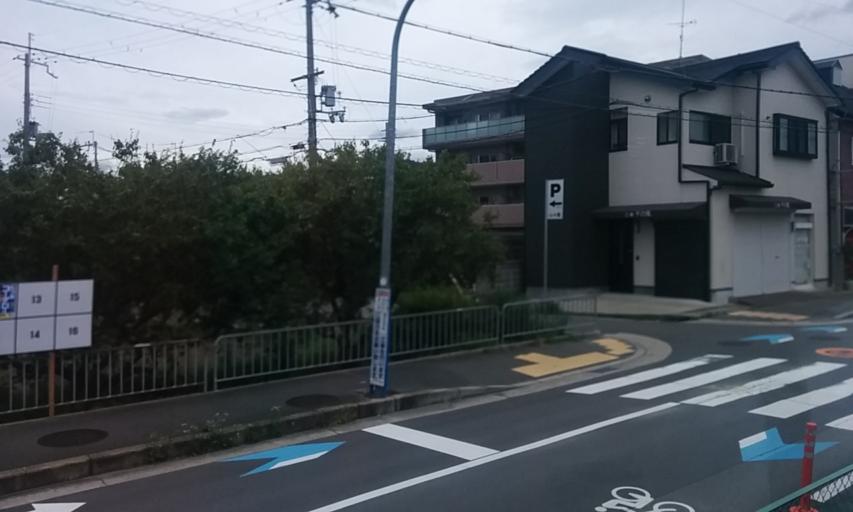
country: JP
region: Osaka
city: Mino
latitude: 34.8216
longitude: 135.4655
